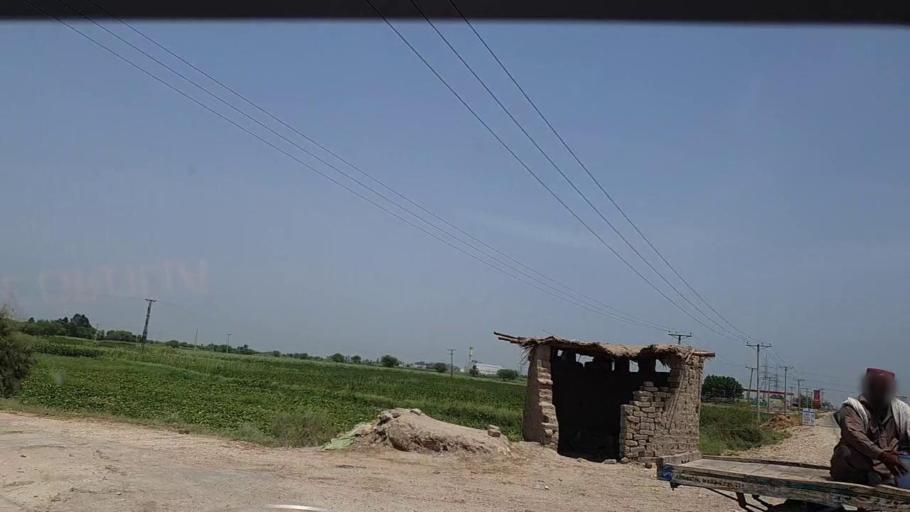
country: PK
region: Sindh
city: Ghotki
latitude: 28.0156
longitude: 69.3551
